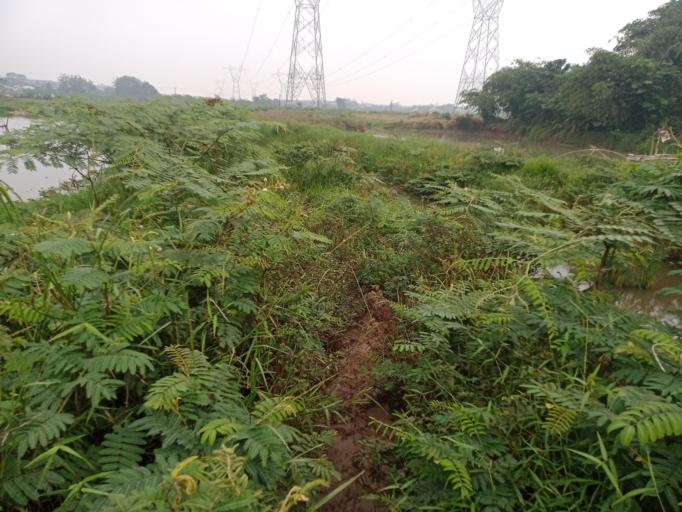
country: ID
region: West Java
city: Cikupa
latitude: -6.2221
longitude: 106.4890
